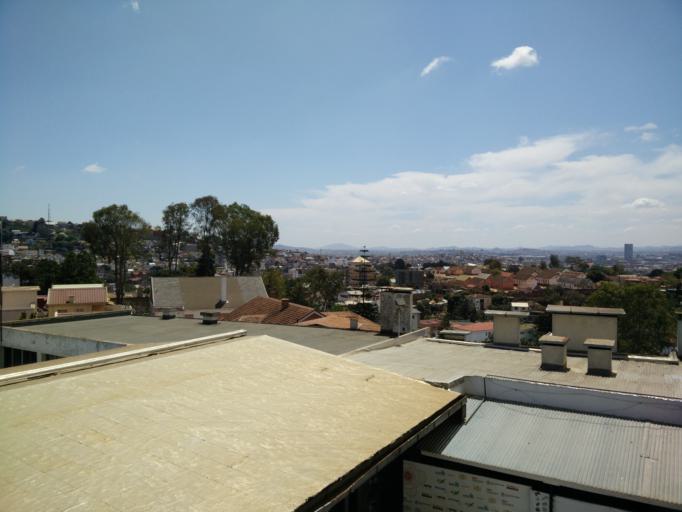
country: MG
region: Analamanga
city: Antananarivo
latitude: -18.9106
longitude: 47.5431
